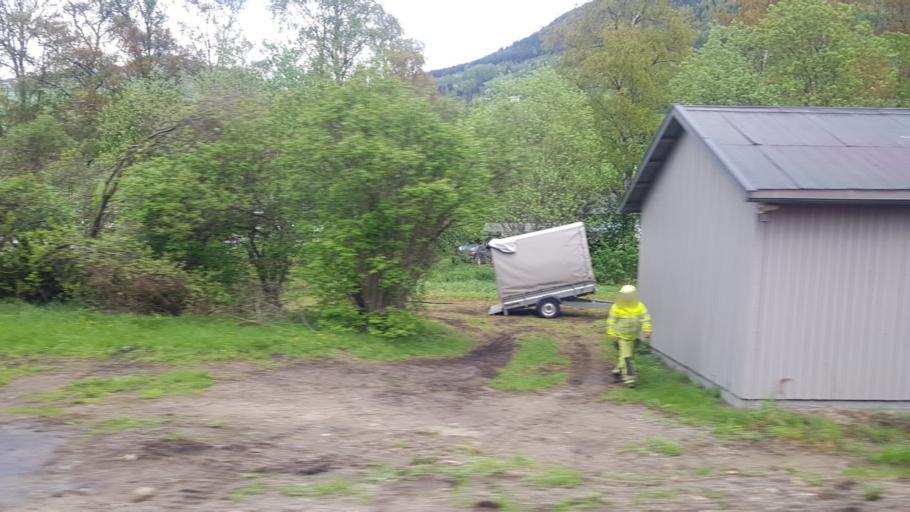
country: NO
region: Oppland
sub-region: Nord-Fron
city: Vinstra
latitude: 61.6641
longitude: 9.6864
